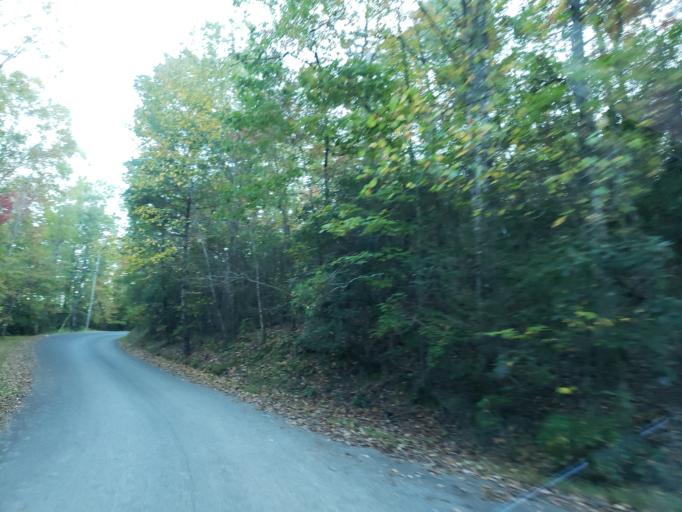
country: US
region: Georgia
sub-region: Gilmer County
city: Ellijay
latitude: 34.6499
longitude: -84.2683
